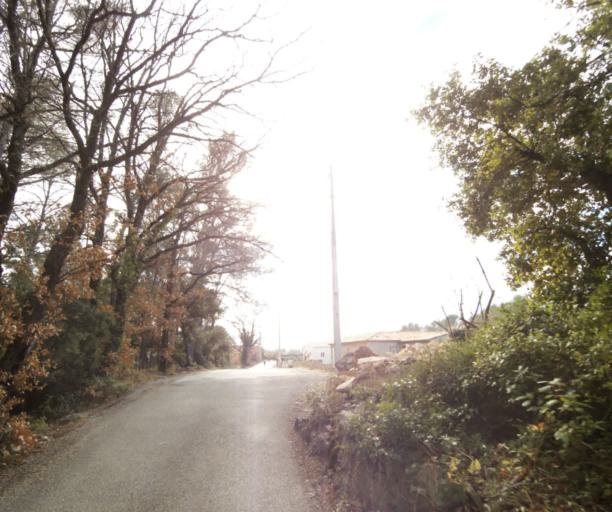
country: FR
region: Provence-Alpes-Cote d'Azur
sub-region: Departement du Var
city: Trans-en-Provence
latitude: 43.5125
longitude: 6.4949
